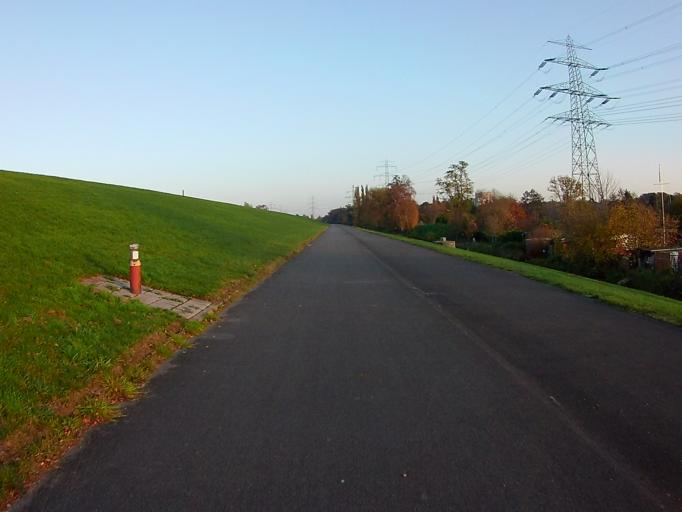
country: DE
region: Hamburg
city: Harburg
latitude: 53.4750
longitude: 9.9427
